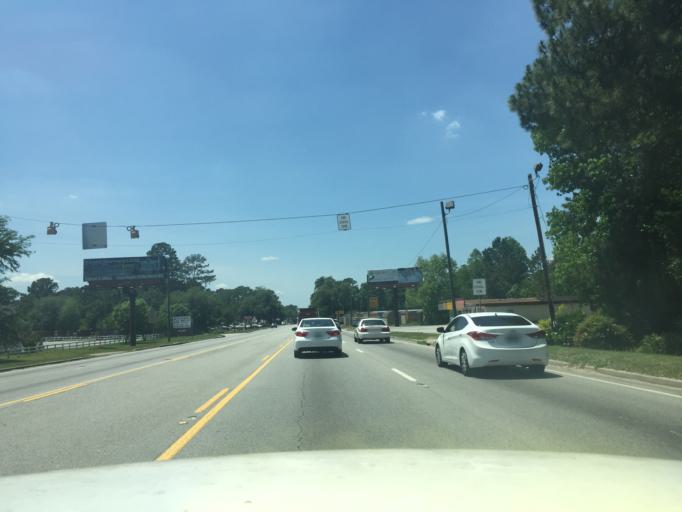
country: US
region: Georgia
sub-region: Chatham County
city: Georgetown
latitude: 32.0435
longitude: -81.1854
